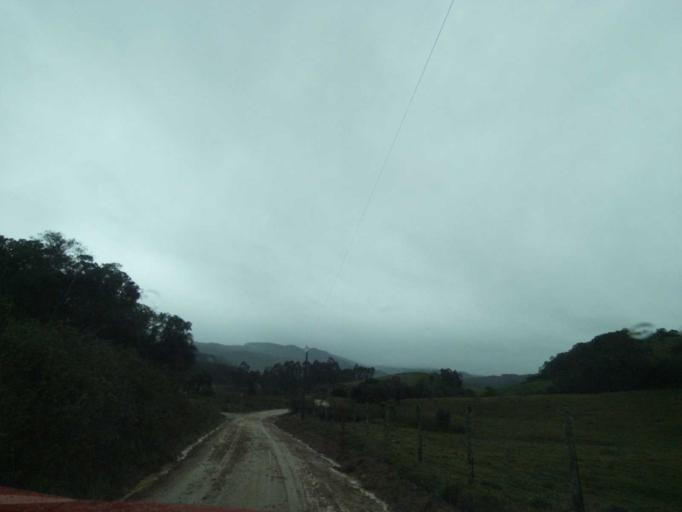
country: BR
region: Santa Catarina
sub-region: Anitapolis
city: Anitapolis
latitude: -27.8893
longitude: -49.1950
